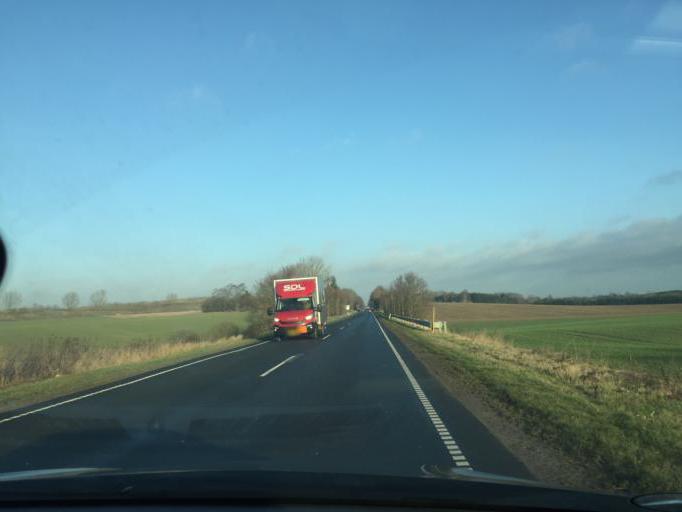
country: DK
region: South Denmark
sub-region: Faaborg-Midtfyn Kommune
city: Faaborg
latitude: 55.1853
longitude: 10.3041
